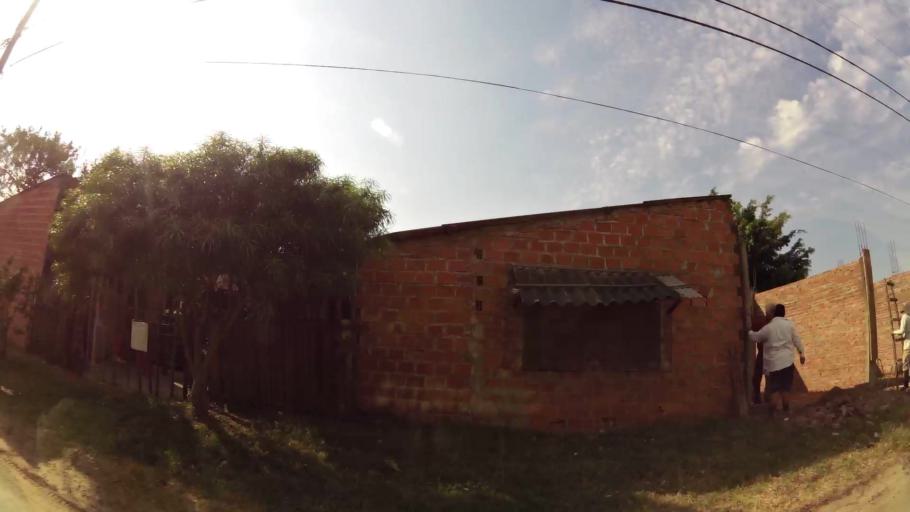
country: BO
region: Santa Cruz
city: Santa Cruz de la Sierra
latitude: -17.7281
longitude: -63.1754
